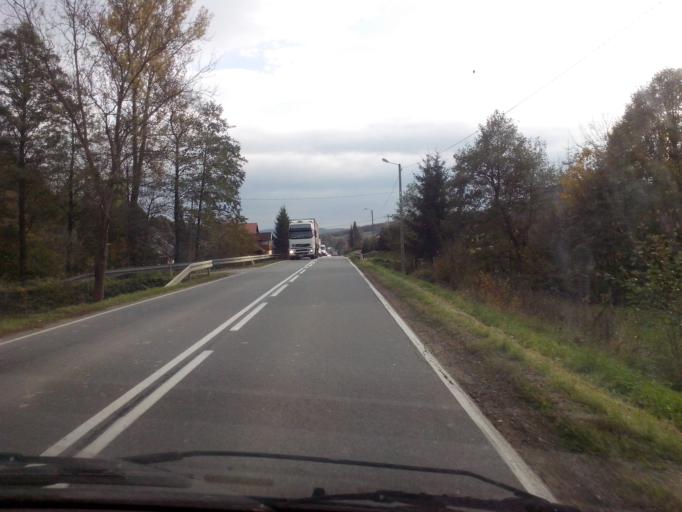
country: PL
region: Subcarpathian Voivodeship
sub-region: Powiat strzyzowski
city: Wisniowa
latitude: 49.8957
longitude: 21.6432
